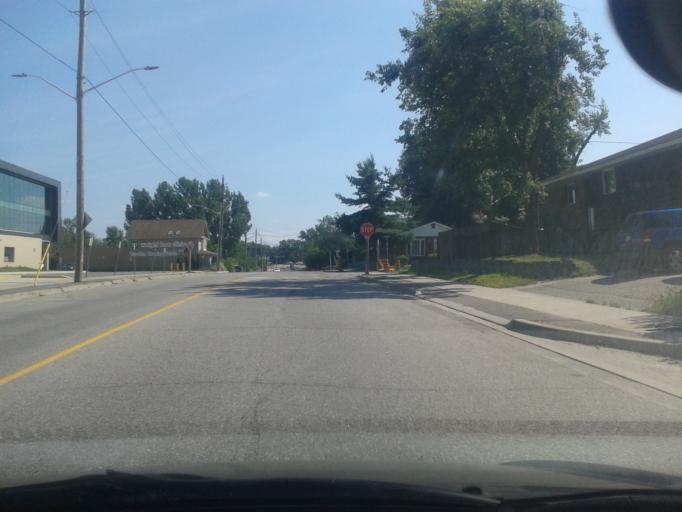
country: CA
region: Ontario
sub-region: Nipissing District
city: North Bay
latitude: 46.3146
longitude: -79.4497
